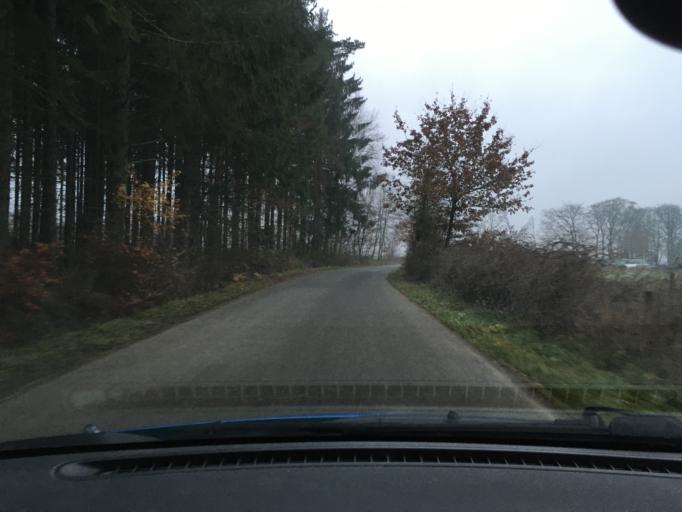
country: DE
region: Lower Saxony
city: Soderstorf
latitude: 53.1536
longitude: 10.1689
